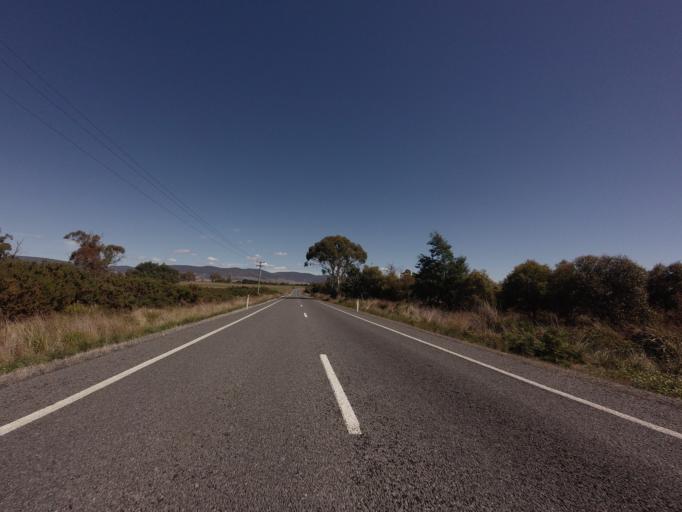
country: AU
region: Tasmania
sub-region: Northern Midlands
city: Evandale
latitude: -41.7739
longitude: 147.7347
